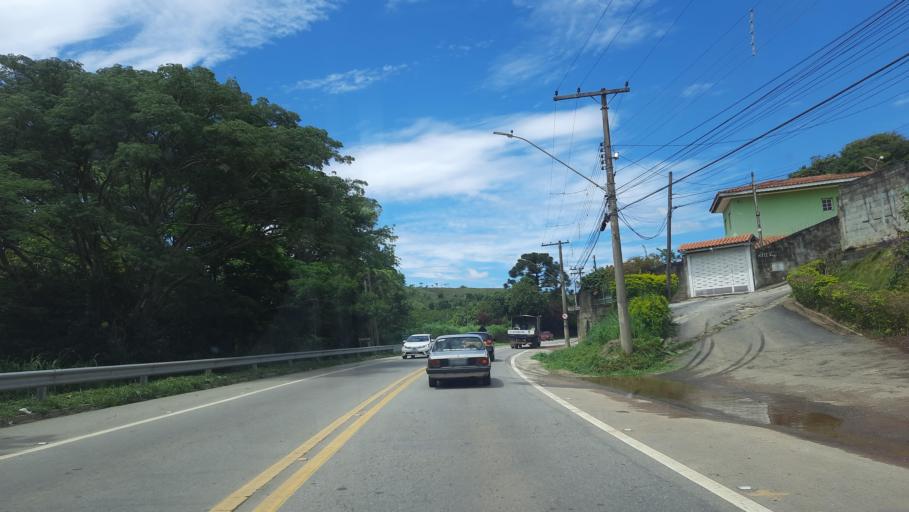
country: BR
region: Sao Paulo
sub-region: Franco Da Rocha
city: Franco da Rocha
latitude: -23.3321
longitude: -46.7058
